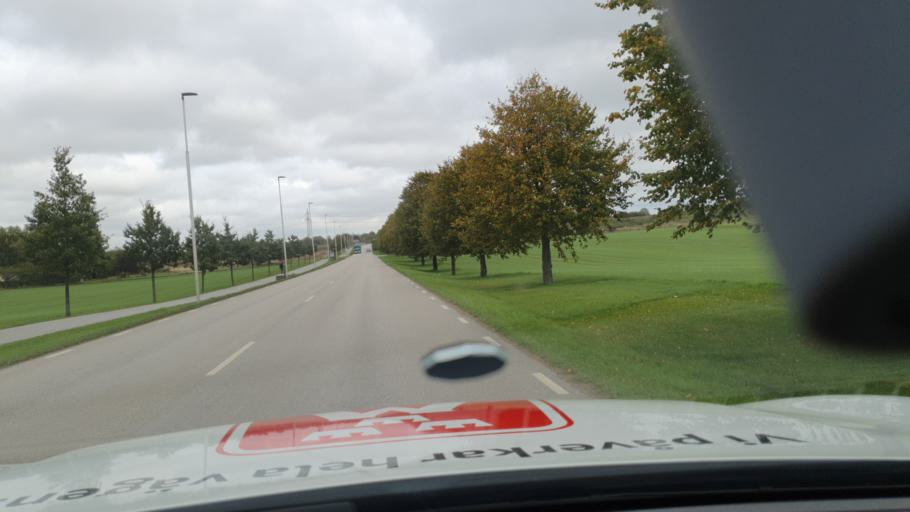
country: SE
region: Skane
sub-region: Burlovs Kommun
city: Arloev
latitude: 55.6439
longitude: 13.0961
